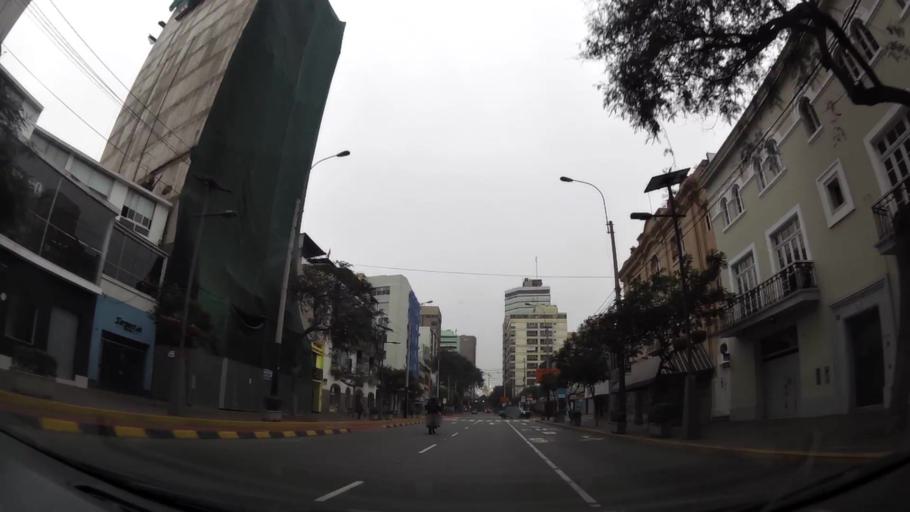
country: PE
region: Lima
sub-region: Lima
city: San Isidro
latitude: -12.1265
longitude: -77.0295
